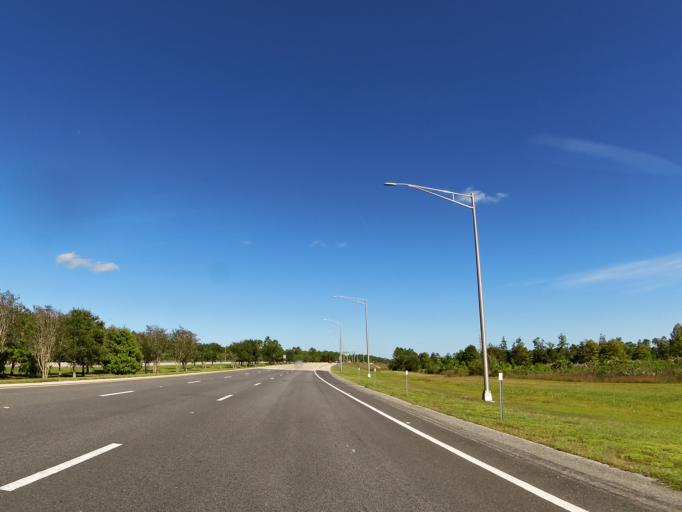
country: US
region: Florida
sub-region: Saint Johns County
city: Palm Valley
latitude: 30.1139
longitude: -81.4383
